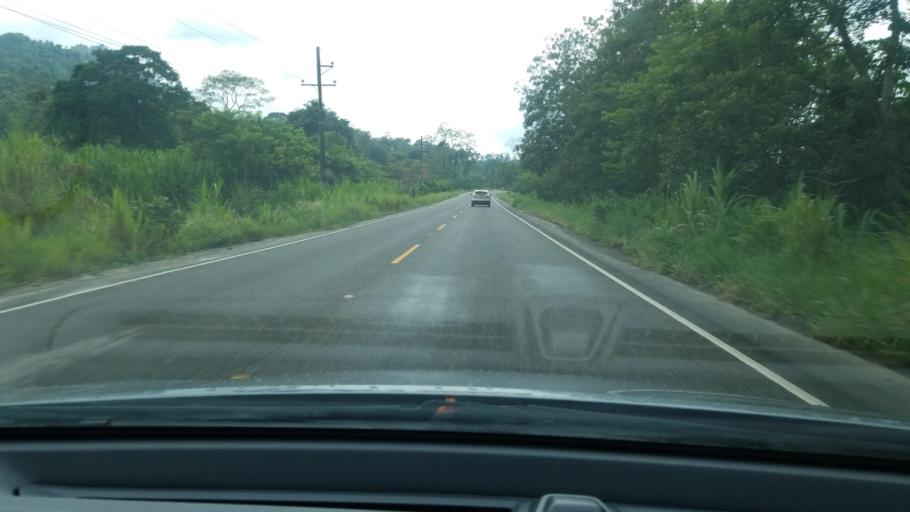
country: HN
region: Cortes
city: Potrerillos
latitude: 15.6129
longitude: -88.2812
